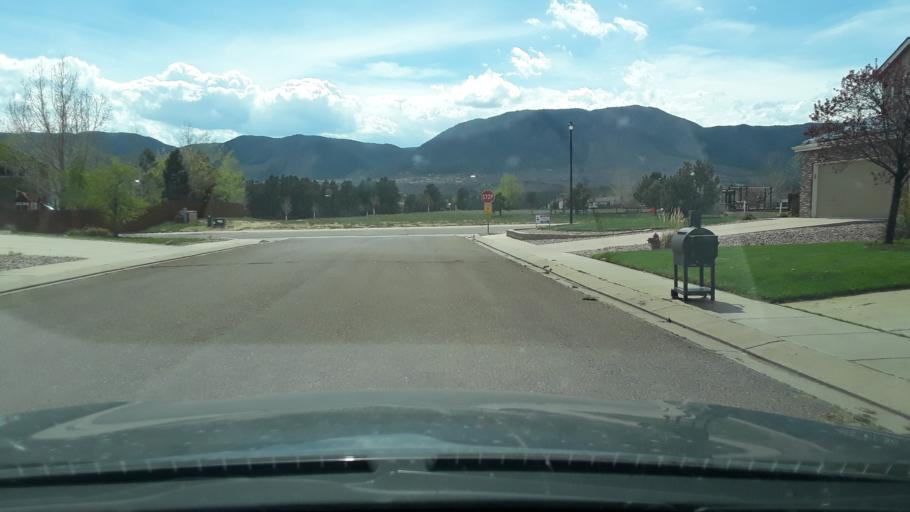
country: US
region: Colorado
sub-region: El Paso County
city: Monument
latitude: 39.0789
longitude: -104.8679
